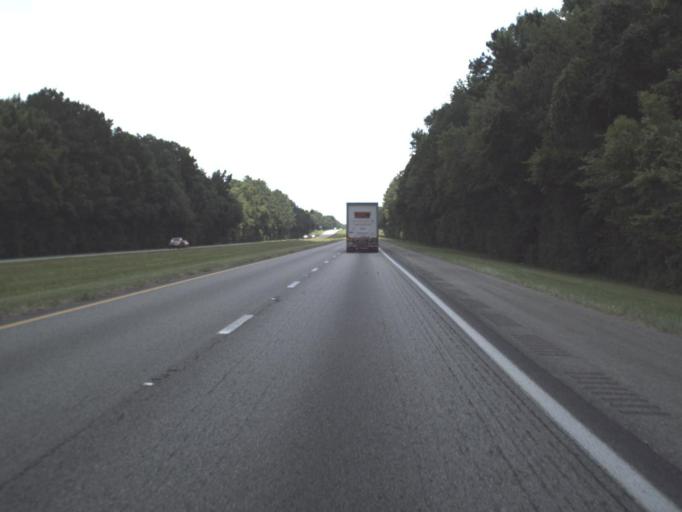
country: US
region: Florida
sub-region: Jefferson County
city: Monticello
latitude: 30.4452
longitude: -83.7208
